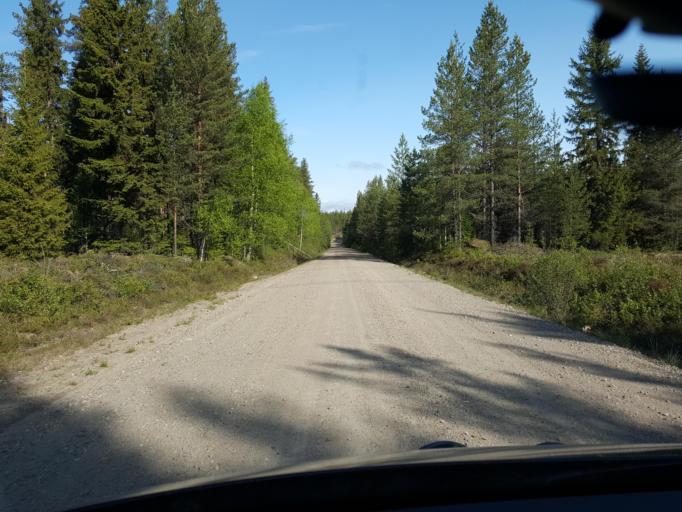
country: SE
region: Vaesternorrland
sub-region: Ange Kommun
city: Ange
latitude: 62.1881
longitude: 15.5985
